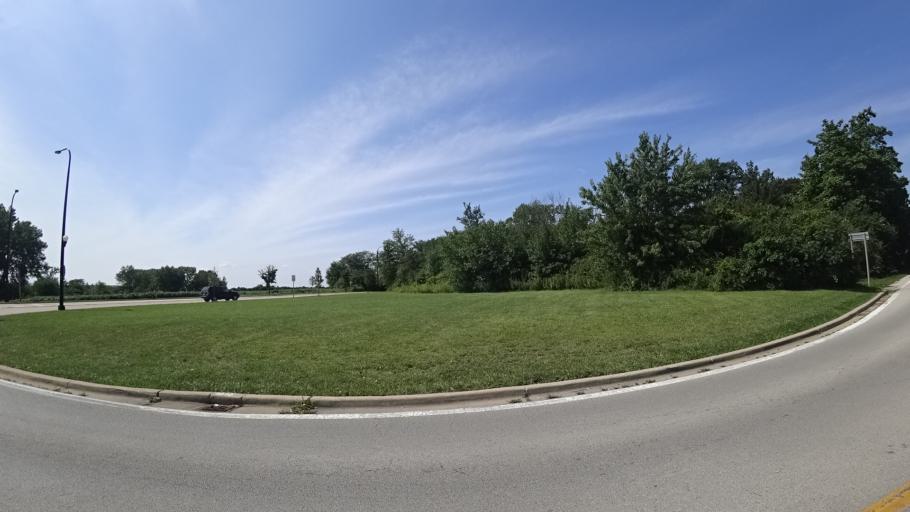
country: US
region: Illinois
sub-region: Cook County
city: Orland Hills
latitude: 41.5588
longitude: -87.8465
